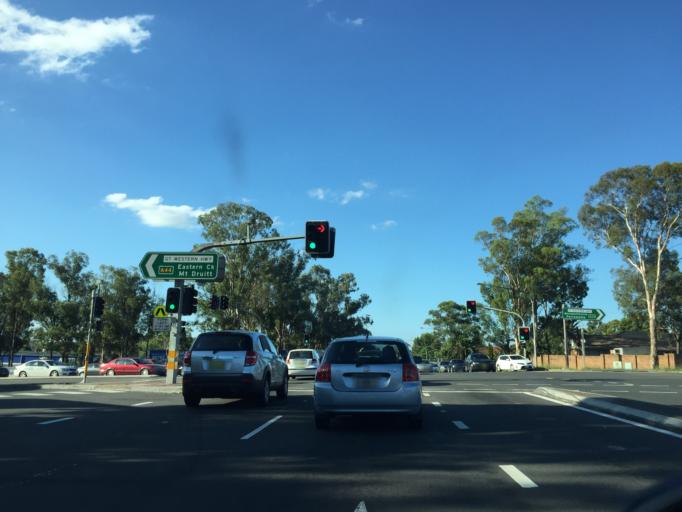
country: AU
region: New South Wales
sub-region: Blacktown
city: Blacktown
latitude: -33.7984
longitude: 150.8968
